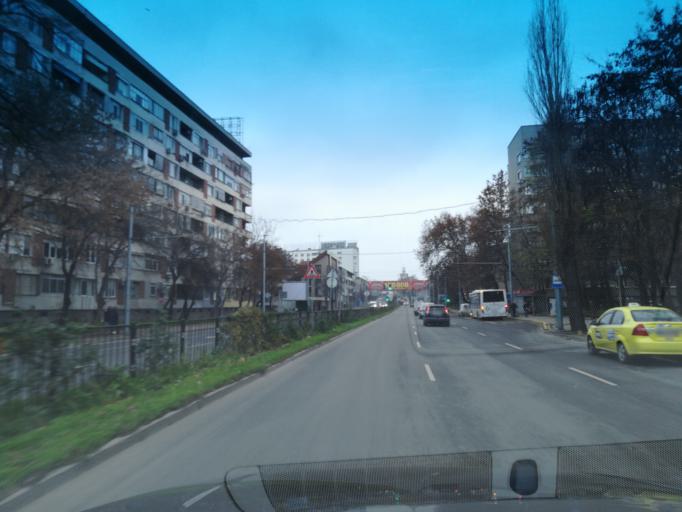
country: BG
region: Plovdiv
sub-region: Obshtina Plovdiv
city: Plovdiv
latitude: 42.1624
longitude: 24.7475
